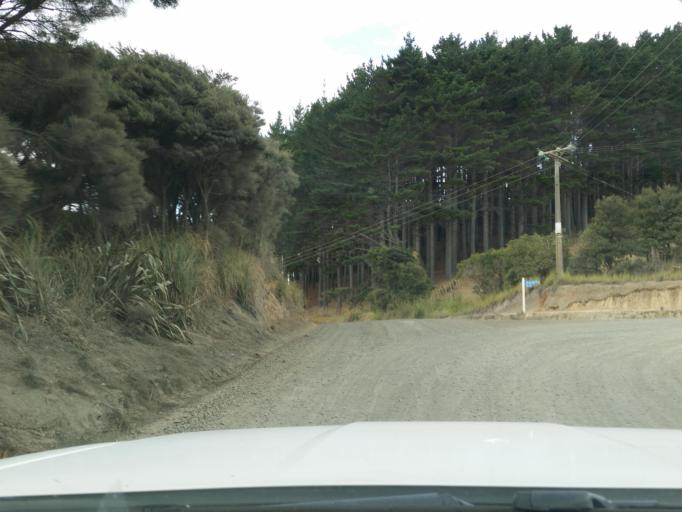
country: NZ
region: Auckland
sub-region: Auckland
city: Wellsford
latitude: -36.3009
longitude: 174.1107
